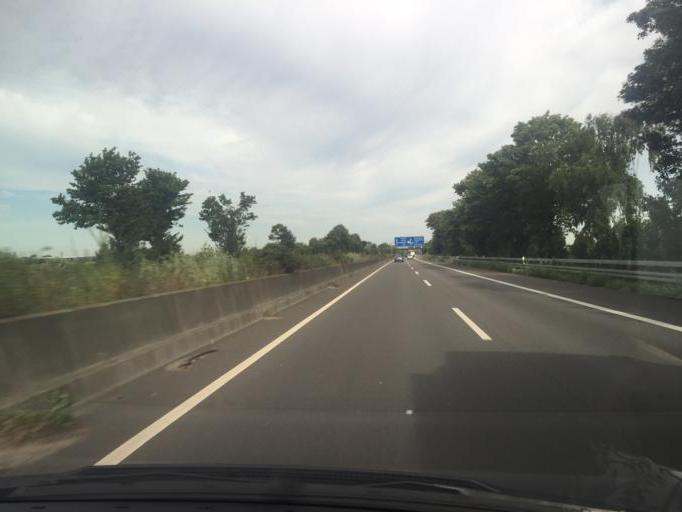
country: DE
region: North Rhine-Westphalia
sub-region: Regierungsbezirk Dusseldorf
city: Dormagen
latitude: 51.1409
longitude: 6.7732
